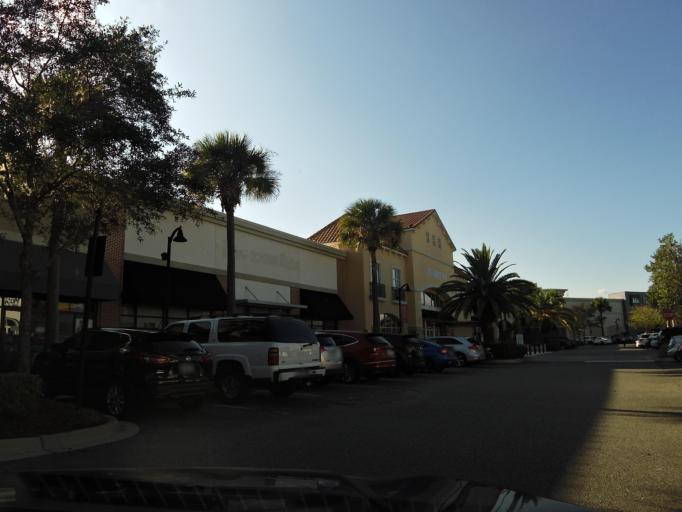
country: US
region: Florida
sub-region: Duval County
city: Jacksonville Beach
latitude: 30.2526
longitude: -81.5311
